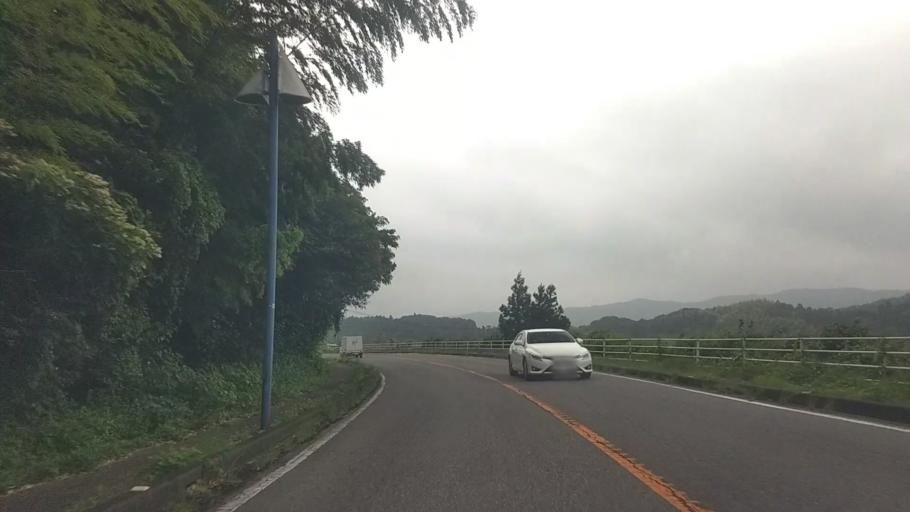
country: JP
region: Chiba
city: Kawaguchi
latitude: 35.1389
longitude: 140.0700
